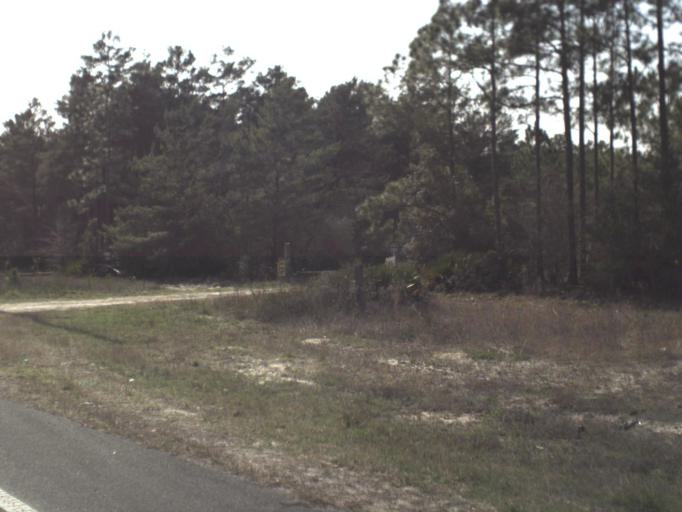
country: US
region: Florida
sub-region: Franklin County
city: Carrabelle
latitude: 29.9329
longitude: -84.5098
